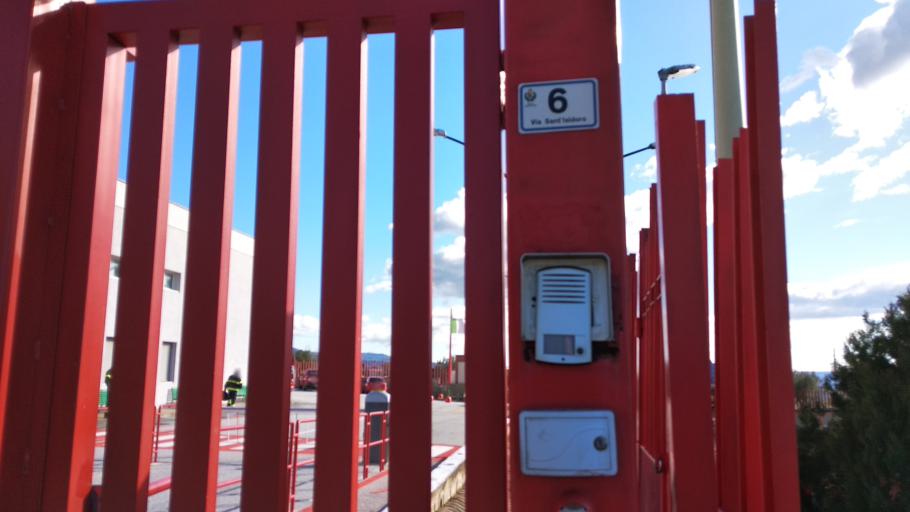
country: IT
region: Calabria
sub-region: Provincia di Catanzaro
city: Santa Eufemia Lamezia
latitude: 38.9602
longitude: 16.2550
